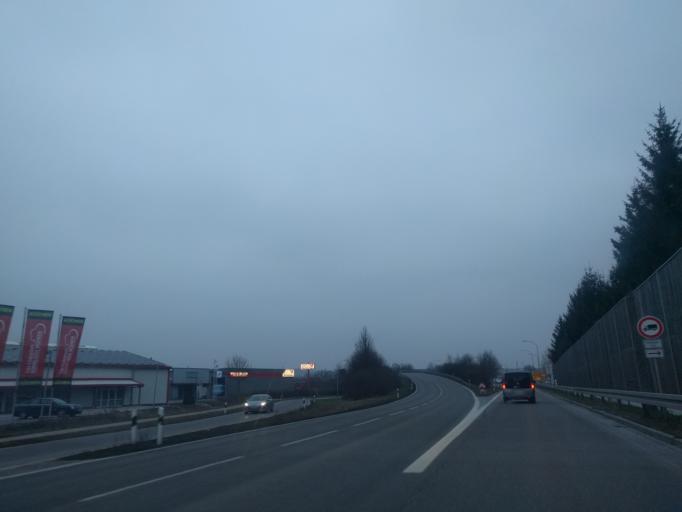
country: DE
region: Bavaria
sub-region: Swabia
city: Donauwoerth
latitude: 48.7095
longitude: 10.7607
